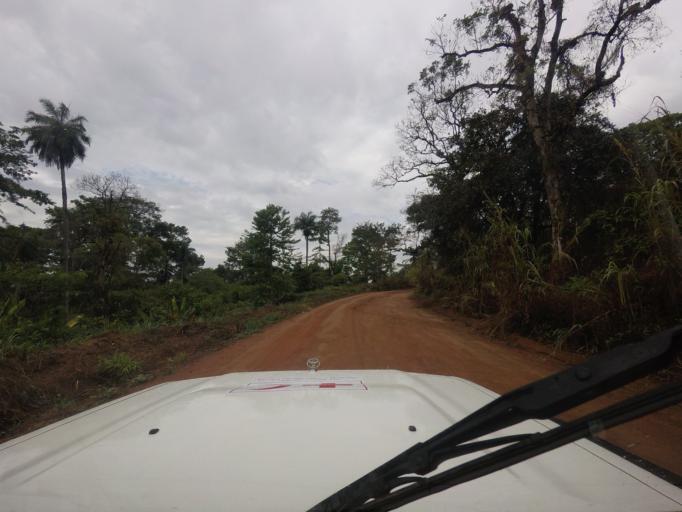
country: SL
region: Eastern Province
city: Buedu
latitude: 8.3446
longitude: -10.1786
